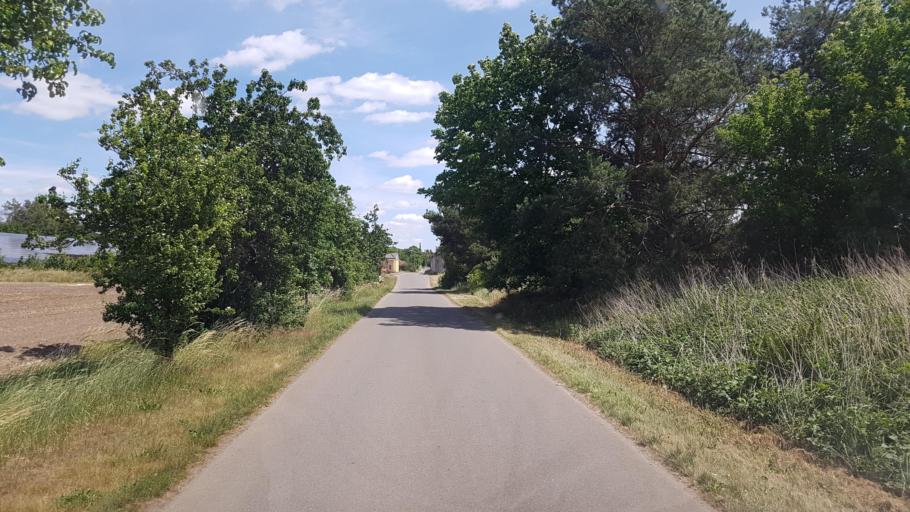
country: DE
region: Brandenburg
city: Hohenleipisch
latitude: 51.4748
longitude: 13.5680
